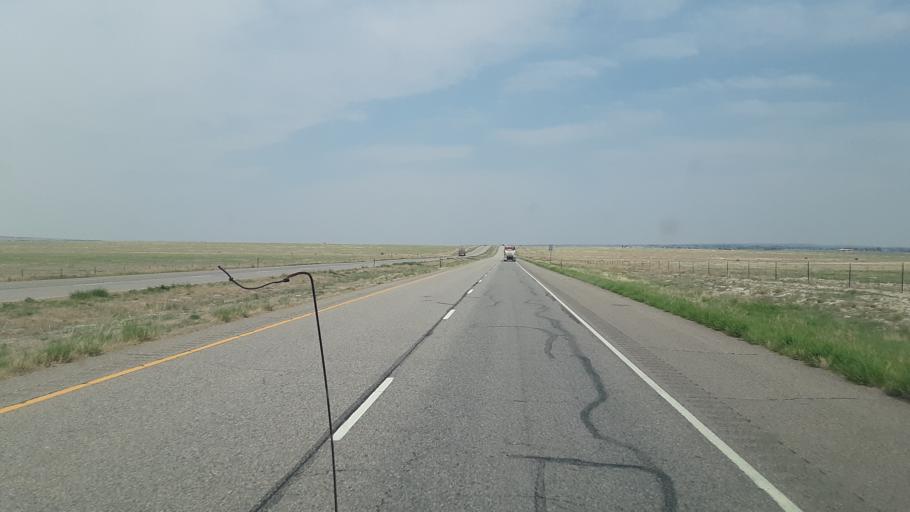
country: US
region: Colorado
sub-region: Pueblo County
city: Pueblo West
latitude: 38.3591
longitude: -104.8646
